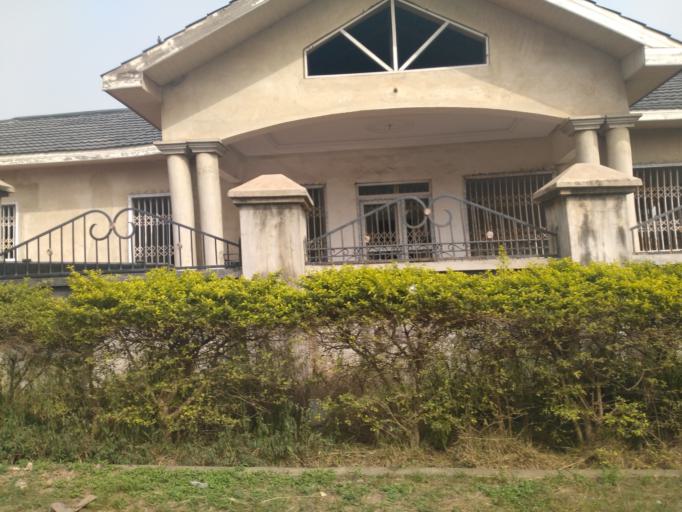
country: GH
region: Ashanti
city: Kumasi
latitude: 6.6793
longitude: -1.6045
